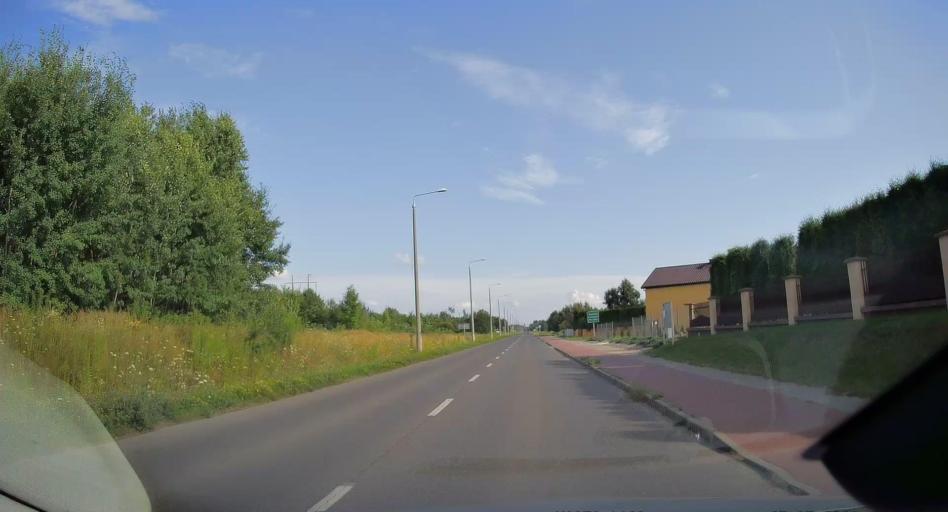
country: PL
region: Swietokrzyskie
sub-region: Powiat konecki
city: Konskie
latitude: 51.2150
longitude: 20.3922
